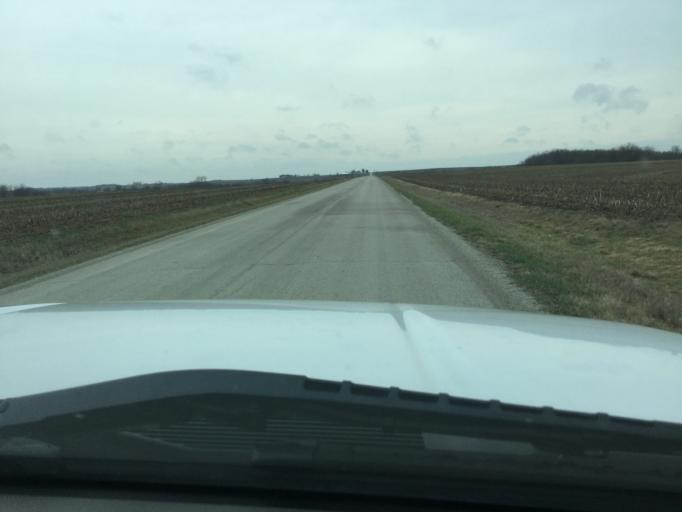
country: US
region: Kansas
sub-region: Nemaha County
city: Sabetha
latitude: 39.8448
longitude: -95.7142
